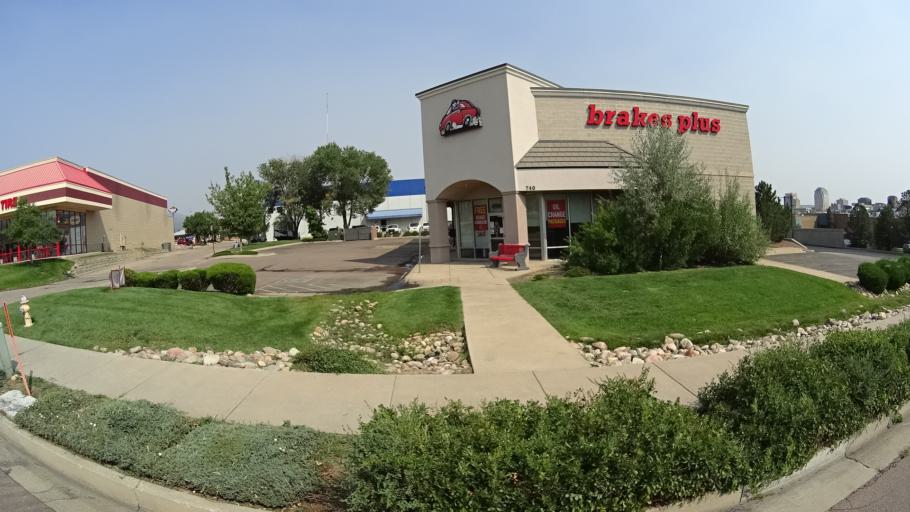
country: US
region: Colorado
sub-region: El Paso County
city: Colorado Springs
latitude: 38.8248
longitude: -104.8382
